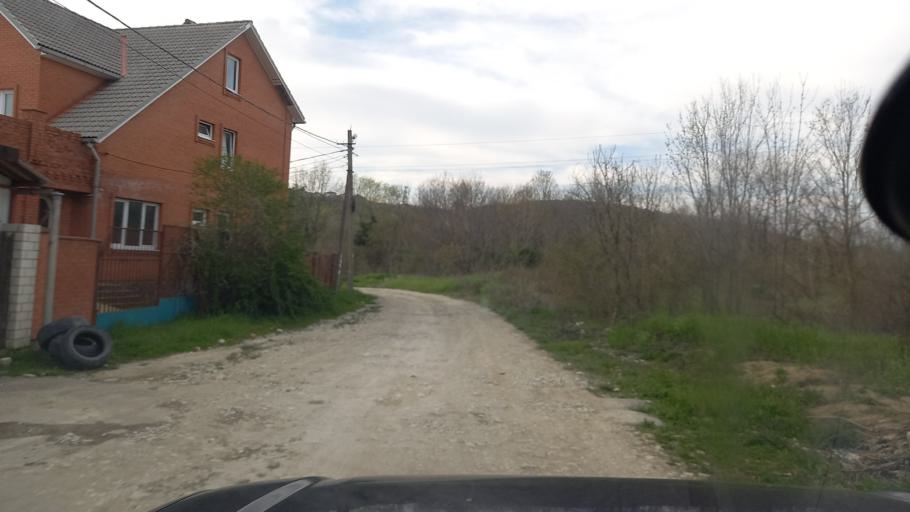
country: RU
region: Krasnodarskiy
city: Arkhipo-Osipovka
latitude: 44.3678
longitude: 38.5476
